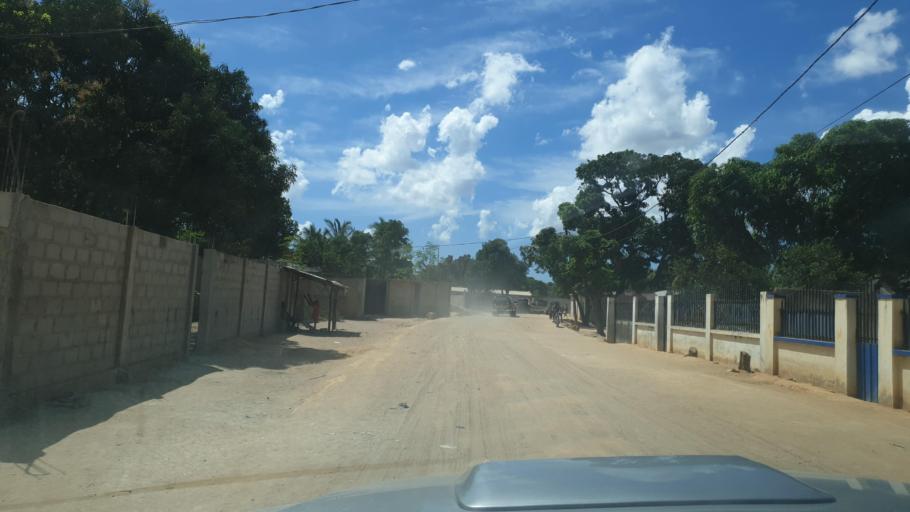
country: MZ
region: Nampula
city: Nacala
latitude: -14.5673
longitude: 40.6971
